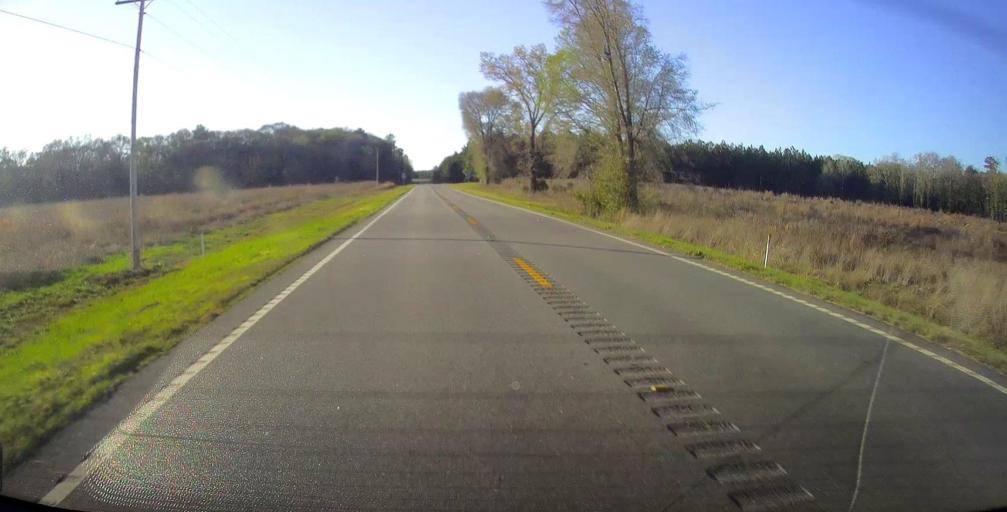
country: US
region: Georgia
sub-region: Pulaski County
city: Hawkinsville
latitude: 32.2587
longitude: -83.4178
